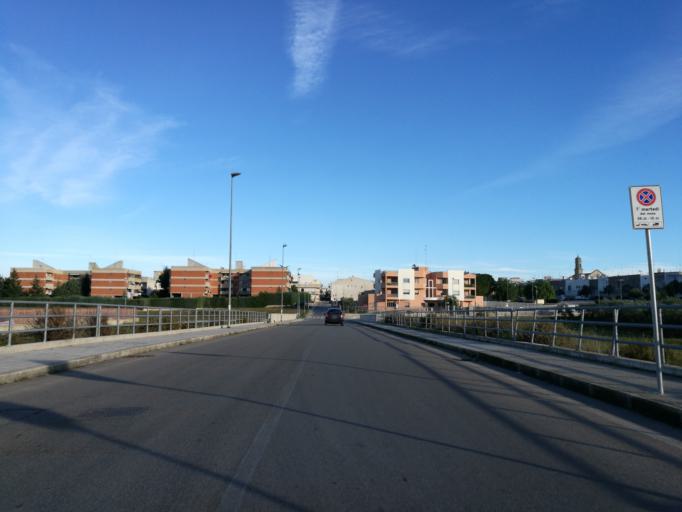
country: IT
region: Apulia
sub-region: Provincia di Bari
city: Adelfia
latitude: 41.0067
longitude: 16.8728
